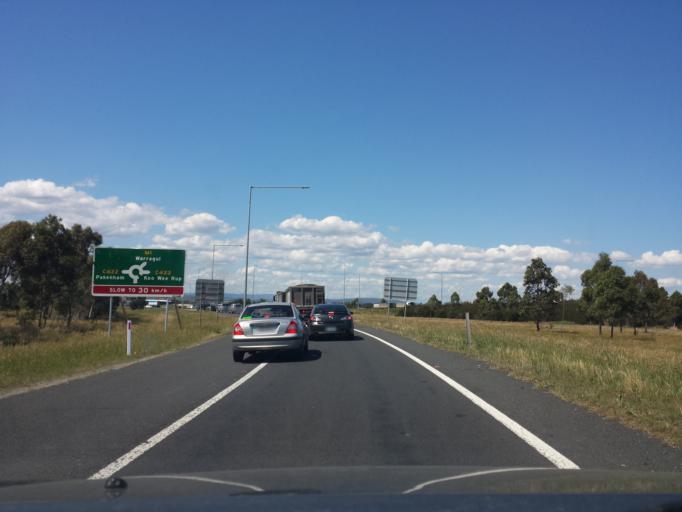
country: AU
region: Victoria
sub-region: Cardinia
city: Pakenham South
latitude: -38.0913
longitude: 145.4883
